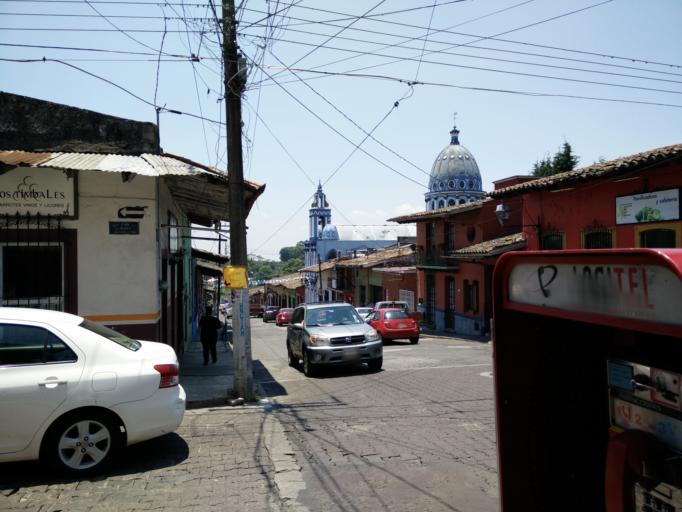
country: MX
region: Veracruz
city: Coatepec
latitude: 19.4527
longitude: -96.9543
